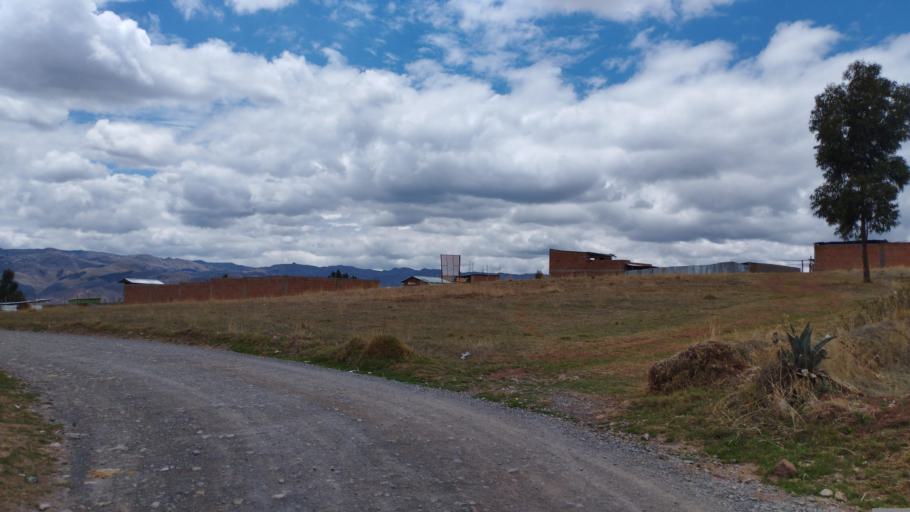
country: PE
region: Cusco
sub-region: Provincia de Cusco
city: Cusco
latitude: -13.5117
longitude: -71.9398
